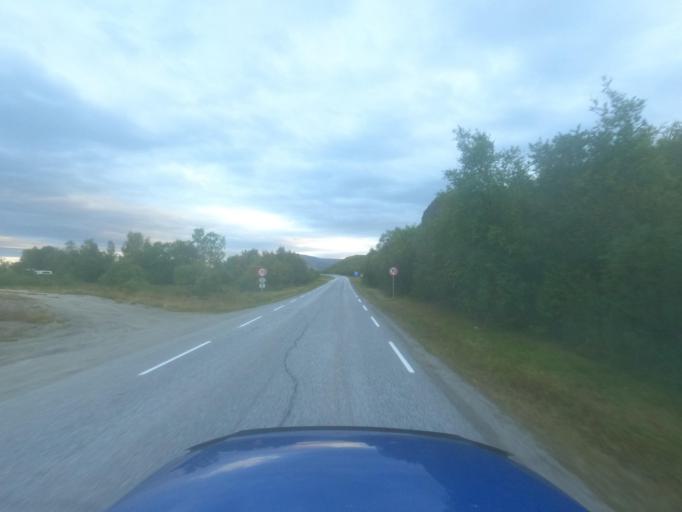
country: NO
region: Finnmark Fylke
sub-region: Porsanger
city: Lakselv
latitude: 70.1847
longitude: 24.9102
